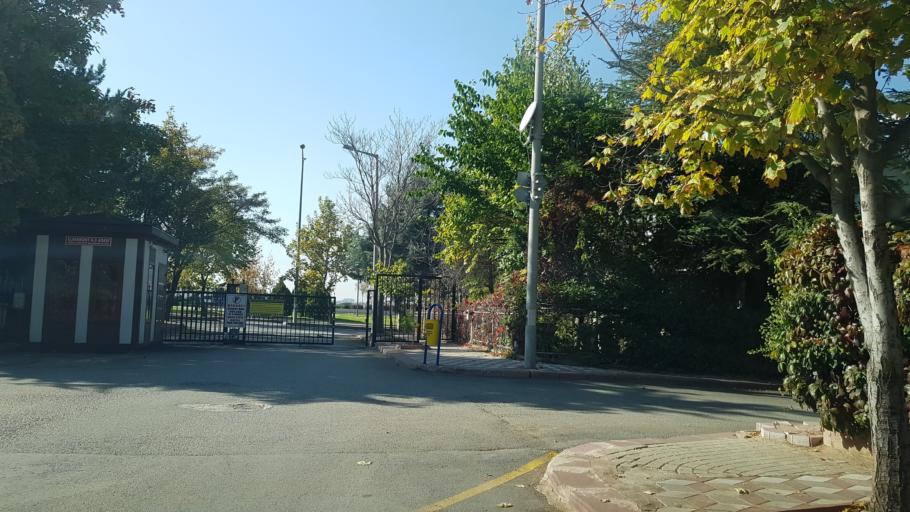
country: TR
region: Ankara
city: Etimesgut
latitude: 39.9511
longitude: 32.6056
